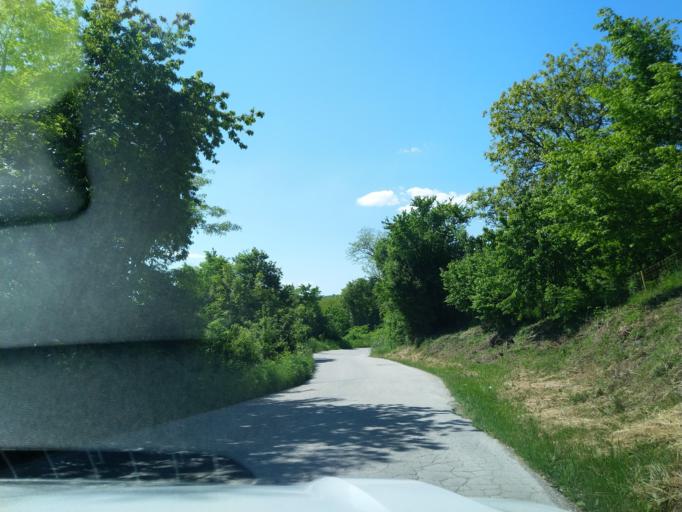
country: RS
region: Central Serbia
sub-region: Zlatiborski Okrug
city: Uzice
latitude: 43.8580
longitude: 19.9130
